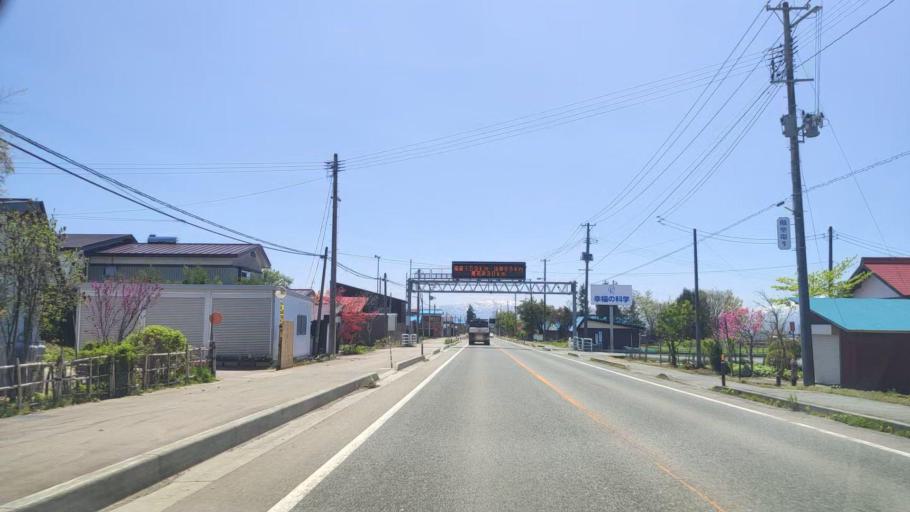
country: JP
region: Yamagata
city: Shinjo
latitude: 38.8183
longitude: 140.3258
